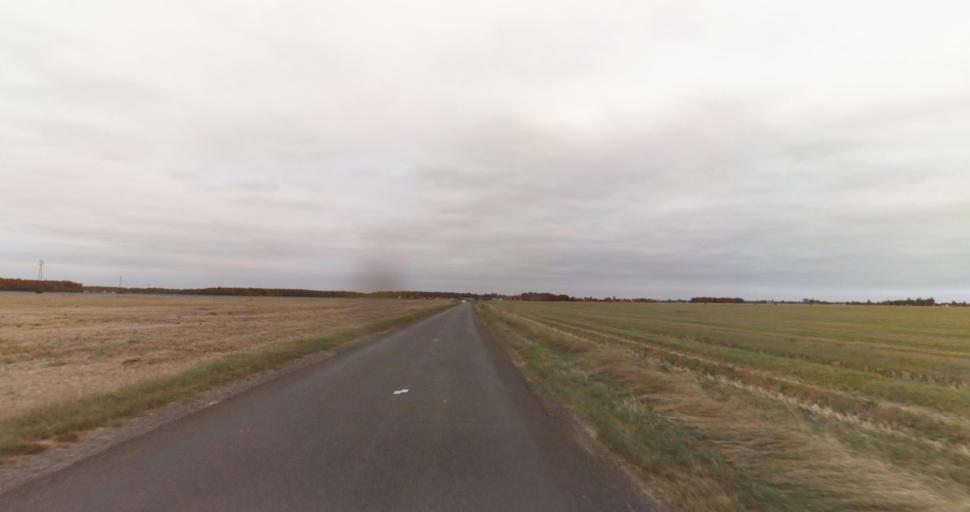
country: FR
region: Centre
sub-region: Departement d'Eure-et-Loir
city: Vert-en-Drouais
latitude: 48.7850
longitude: 1.2920
